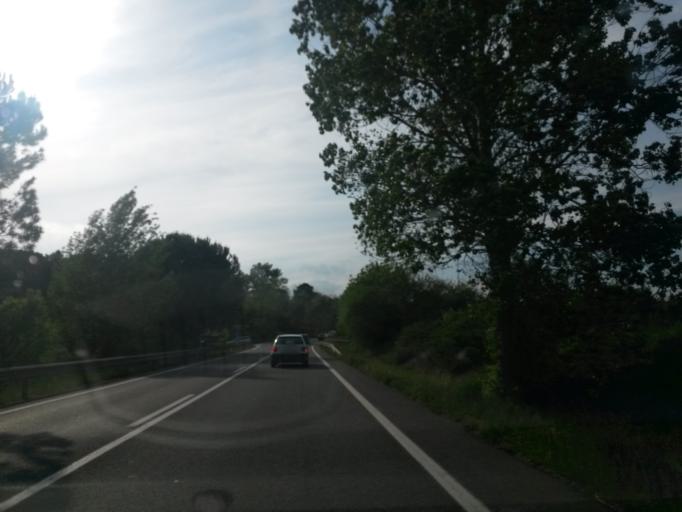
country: ES
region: Catalonia
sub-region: Provincia de Girona
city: Caldes de Malavella
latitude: 41.8413
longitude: 2.7901
